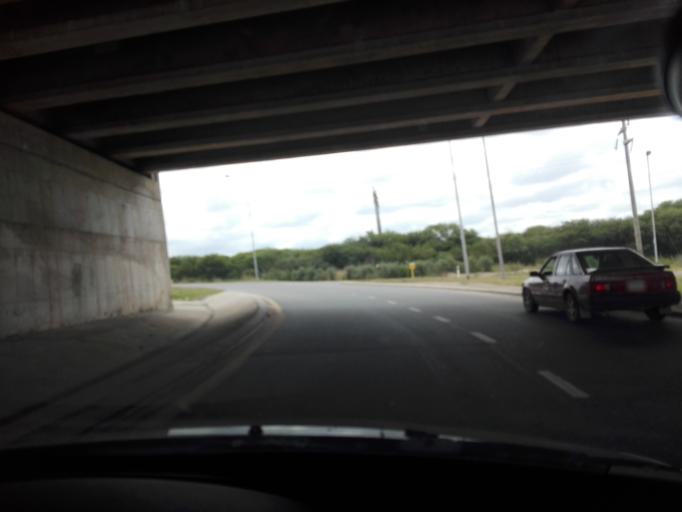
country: AR
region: Cordoba
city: Alta Gracia
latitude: -31.6515
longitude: -64.3148
